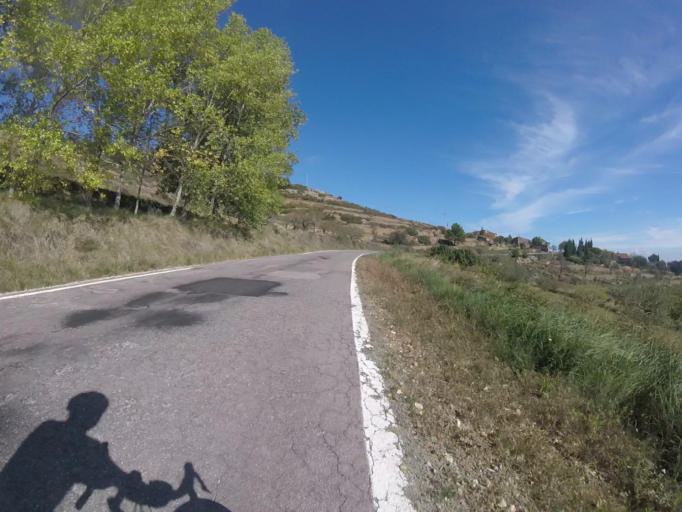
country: ES
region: Valencia
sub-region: Provincia de Castello
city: Sarratella
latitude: 40.3201
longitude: 0.0285
